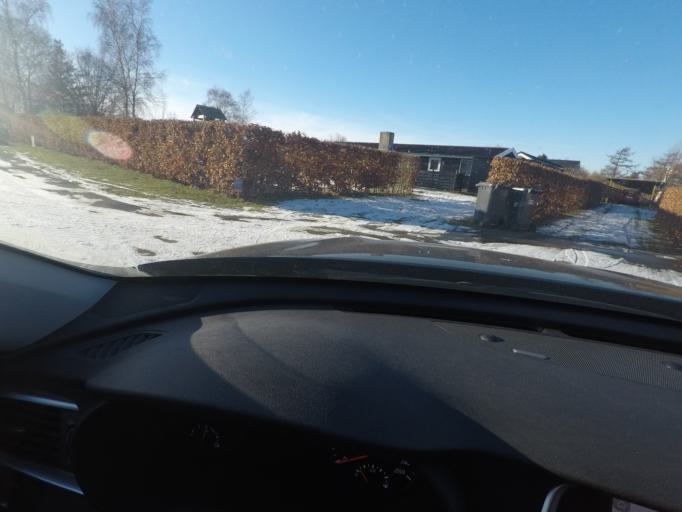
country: DK
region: Capital Region
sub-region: Halsnaes Kommune
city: Liseleje
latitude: 55.9943
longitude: 11.9425
